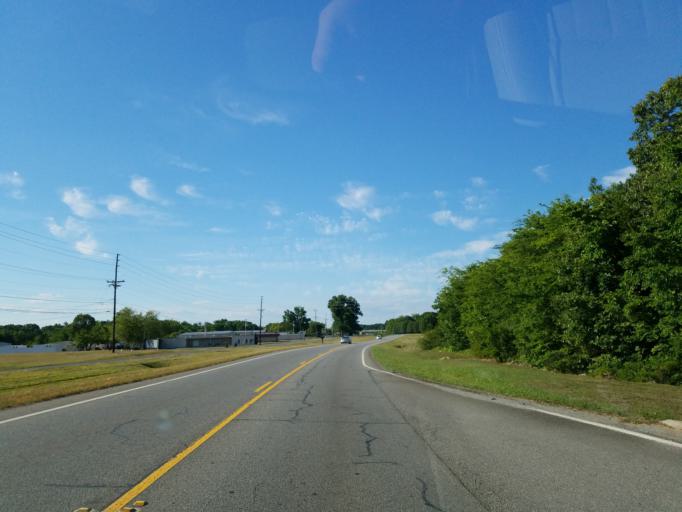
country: US
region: Georgia
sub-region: Gordon County
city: Calhoun
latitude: 34.4539
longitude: -84.9353
